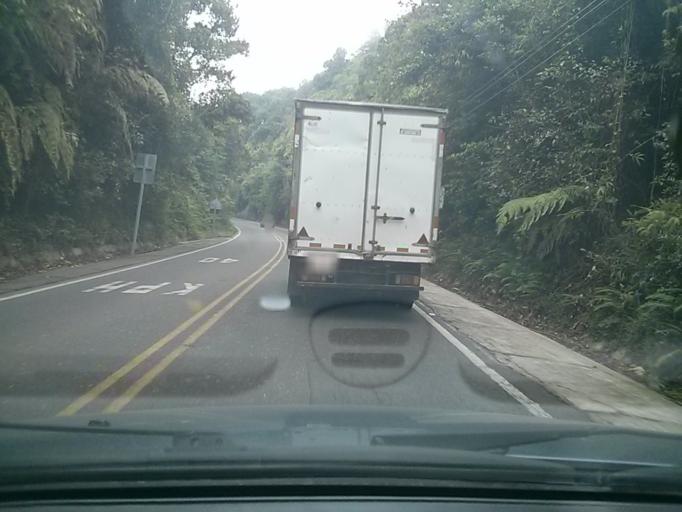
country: CR
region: San Jose
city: San Marcos
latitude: 9.7394
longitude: -83.9576
